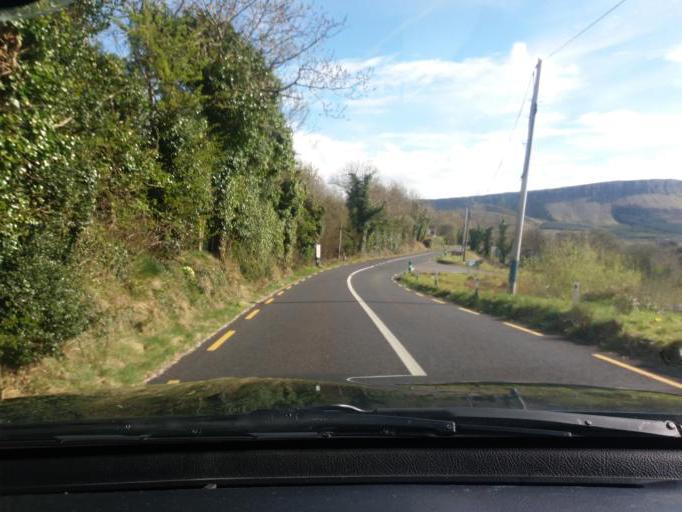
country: IE
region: Connaught
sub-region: County Leitrim
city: Kinlough
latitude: 54.3964
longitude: -8.3035
